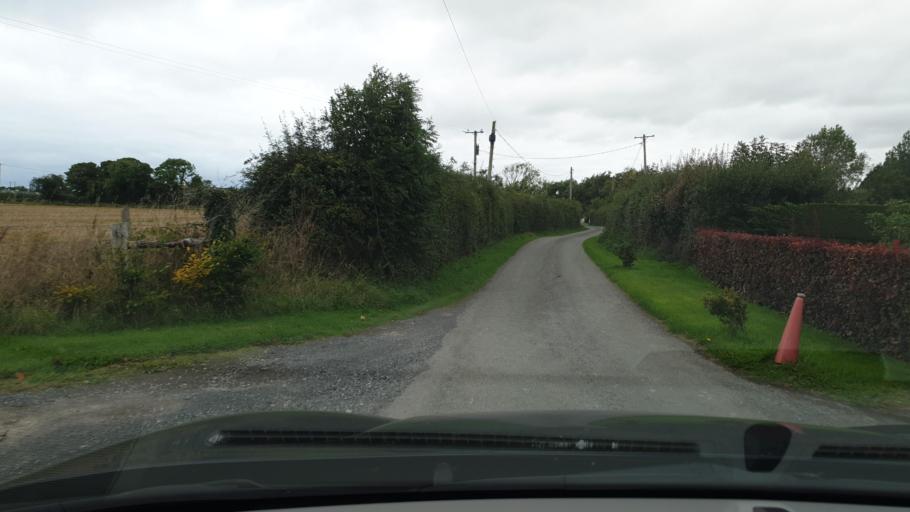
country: IE
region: Leinster
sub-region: Kildare
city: Maynooth
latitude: 53.3388
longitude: -6.6387
